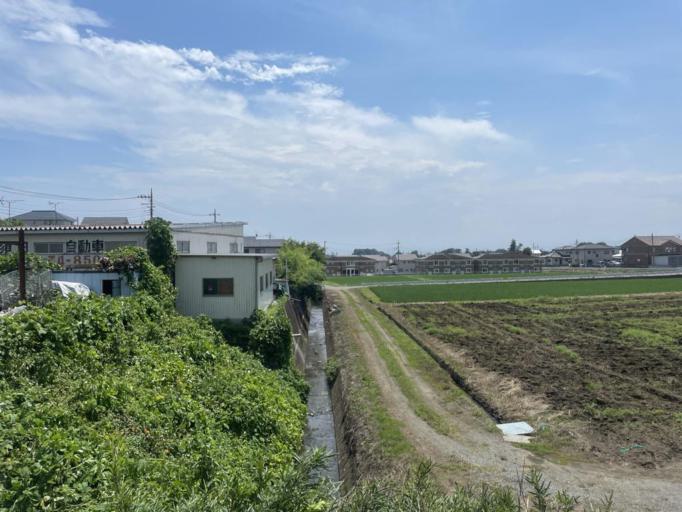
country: JP
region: Gunma
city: Omamacho-omama
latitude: 36.4187
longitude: 139.2349
